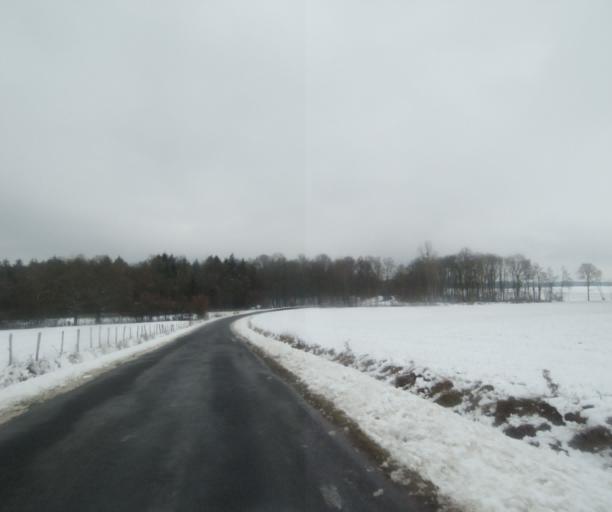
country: FR
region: Champagne-Ardenne
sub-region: Departement de la Haute-Marne
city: Montier-en-Der
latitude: 48.4688
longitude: 4.8135
